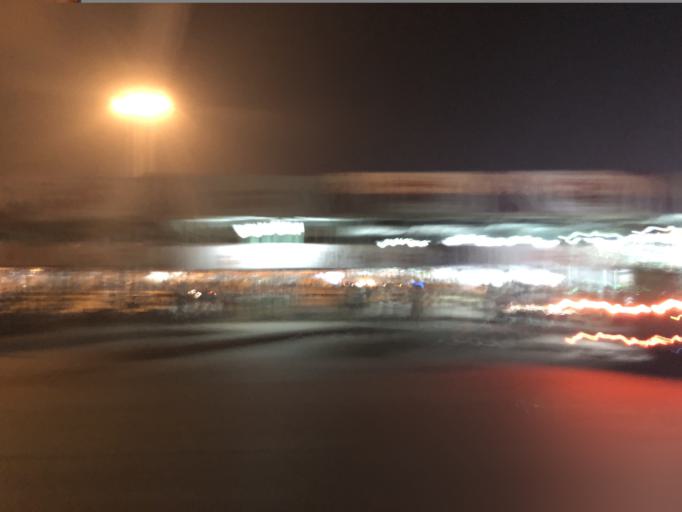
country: IN
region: Tamil Nadu
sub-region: Thanjavur
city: Thanjavur
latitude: 10.7498
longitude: 79.1117
